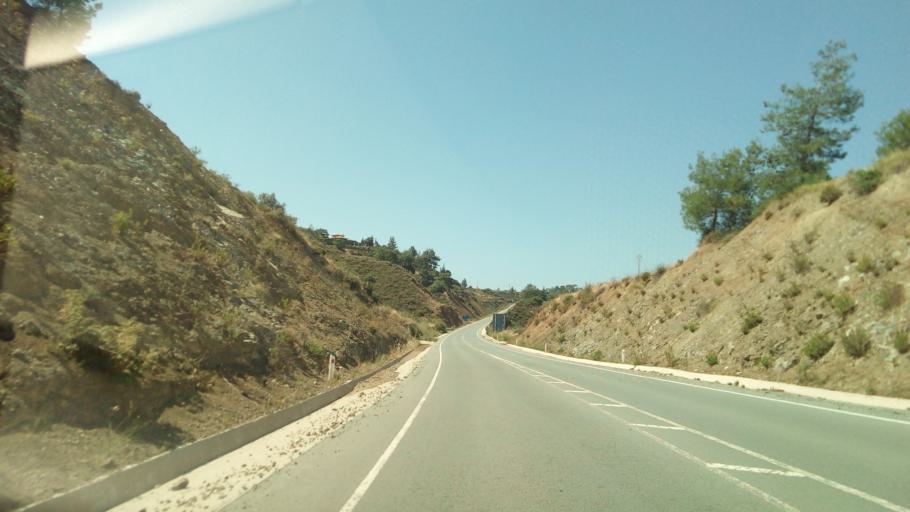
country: CY
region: Limassol
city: Parekklisha
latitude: 34.8142
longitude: 33.1514
